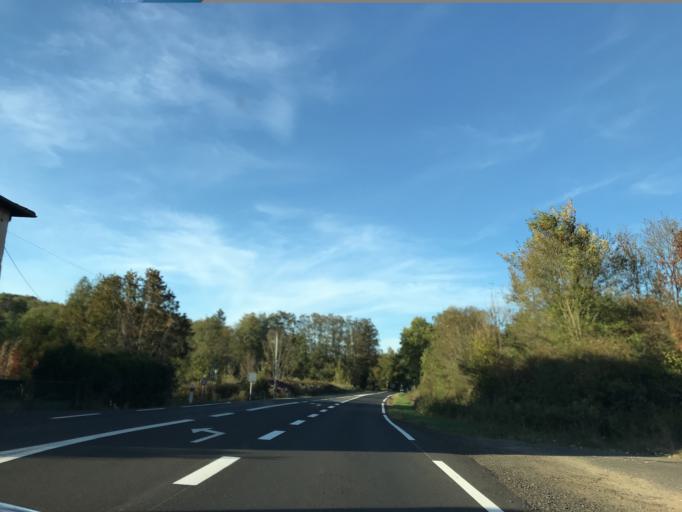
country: FR
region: Auvergne
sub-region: Departement du Puy-de-Dome
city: Thiers
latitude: 45.8812
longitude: 3.5223
